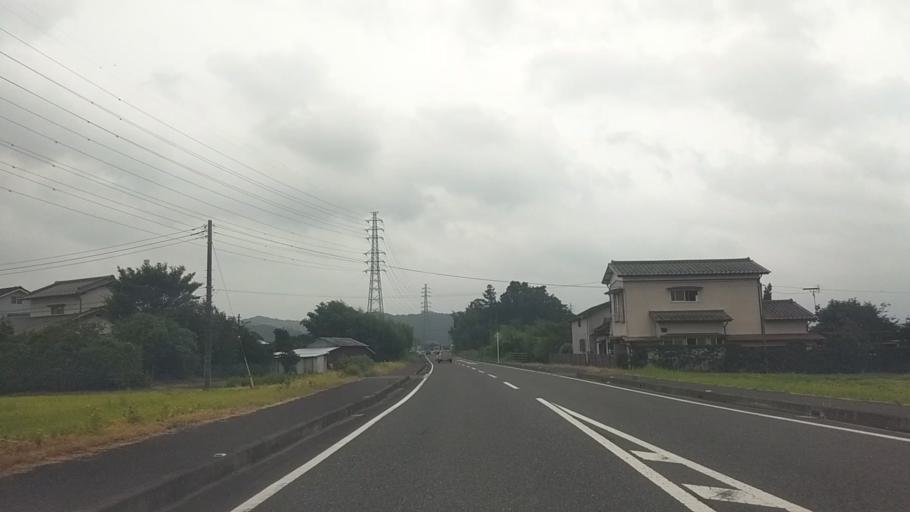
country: JP
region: Chiba
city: Kisarazu
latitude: 35.3130
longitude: 140.0576
